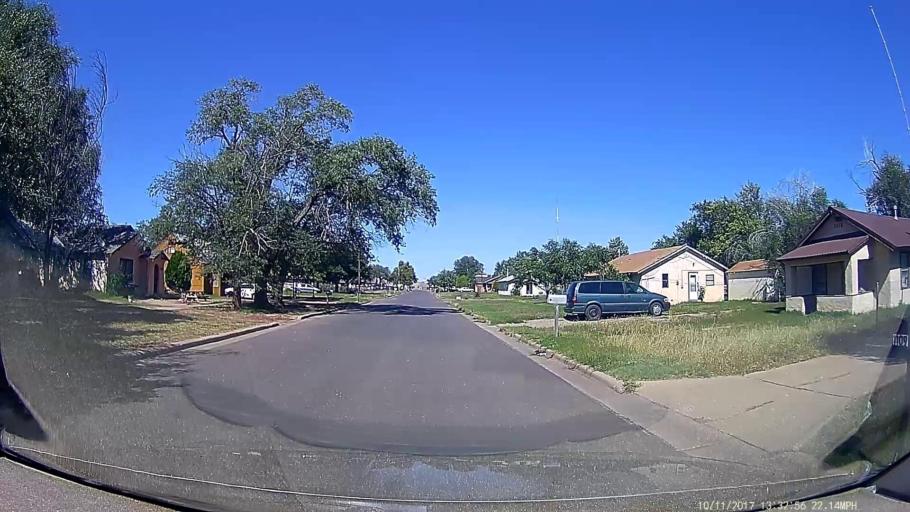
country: US
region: New Mexico
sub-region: Curry County
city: Clovis
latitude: 34.4103
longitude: -103.2105
